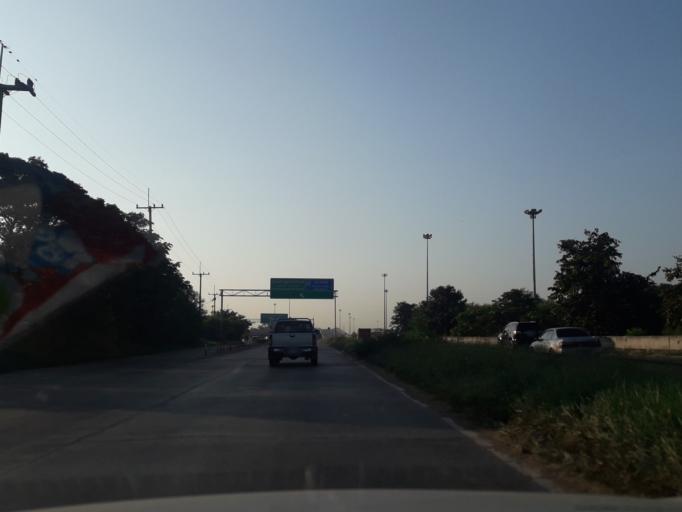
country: TH
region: Phra Nakhon Si Ayutthaya
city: Bang Pa-in
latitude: 14.1615
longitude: 100.5661
